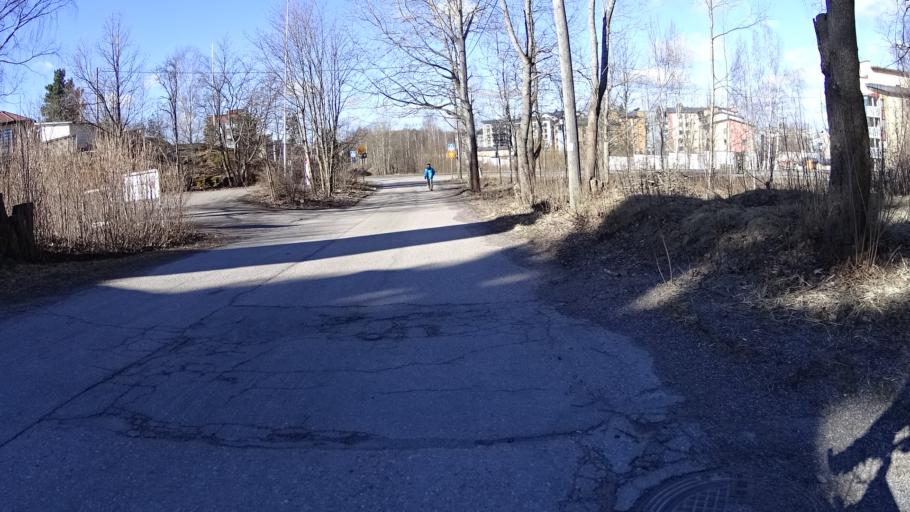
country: FI
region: Uusimaa
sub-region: Helsinki
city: Teekkarikylae
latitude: 60.2566
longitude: 24.8732
